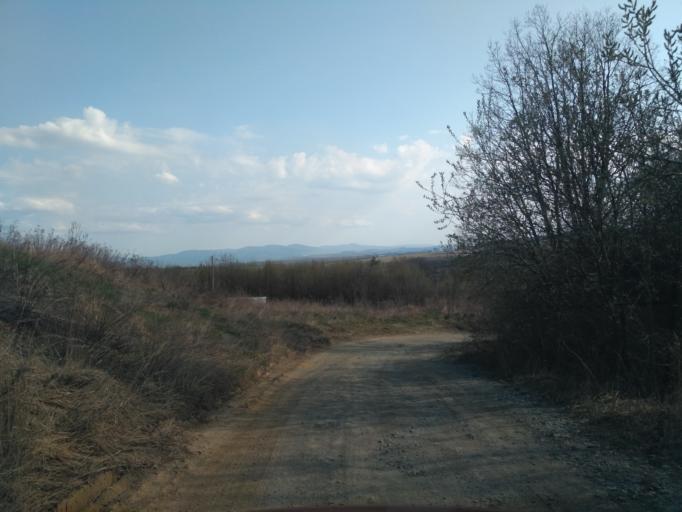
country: SK
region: Kosicky
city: Kosice
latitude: 48.6930
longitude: 21.1949
